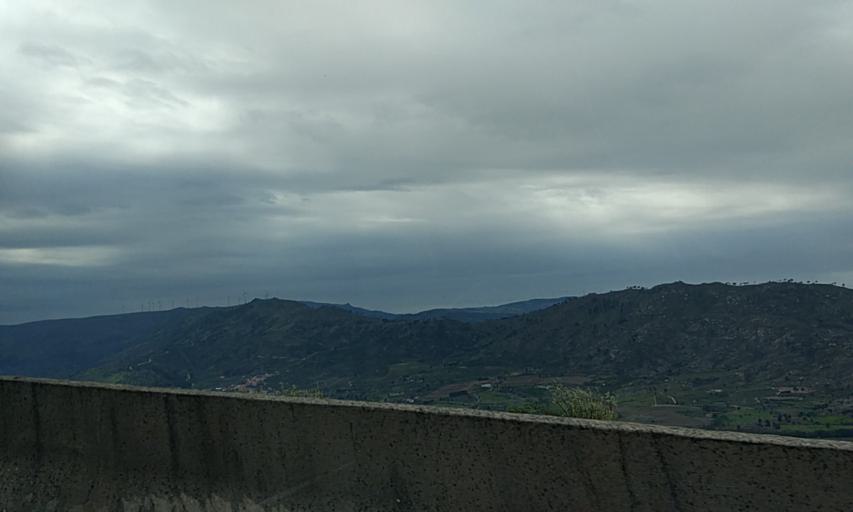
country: PT
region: Guarda
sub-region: Guarda
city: Guarda
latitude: 40.5990
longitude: -7.2754
